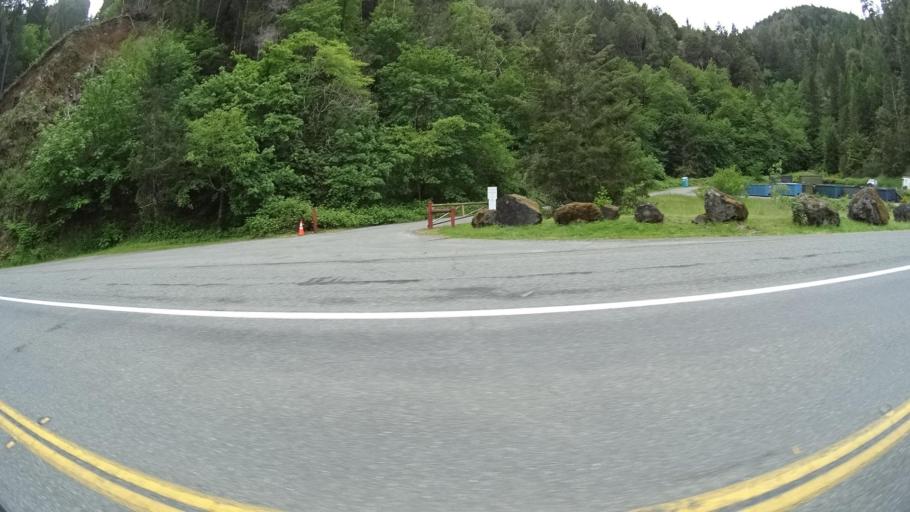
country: US
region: California
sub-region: Humboldt County
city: Willow Creek
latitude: 40.9998
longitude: -123.6462
